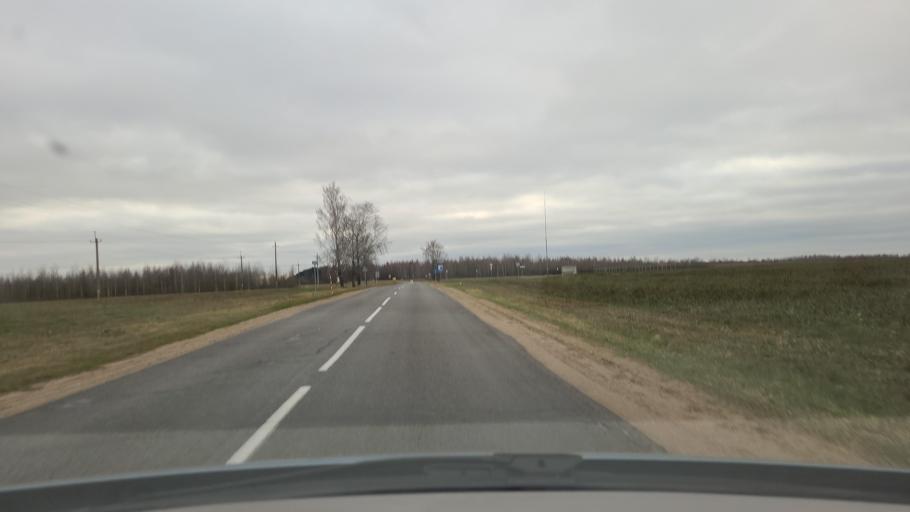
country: BY
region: Minsk
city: Khalopyenichy
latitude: 54.5036
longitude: 28.9574
